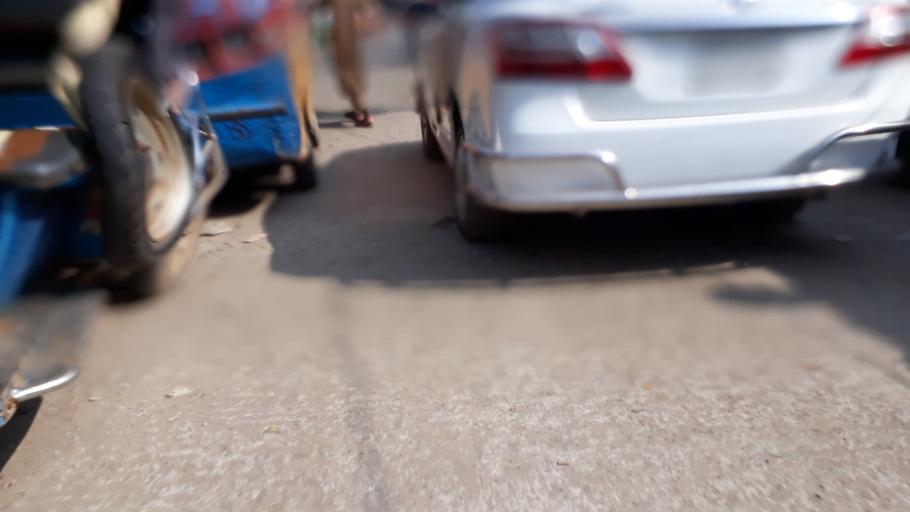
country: BD
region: Dhaka
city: Tungi
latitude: 23.8575
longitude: 90.3112
